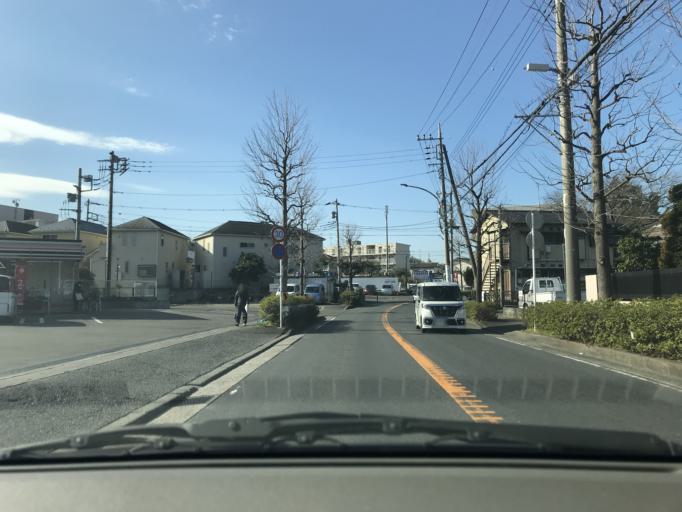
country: JP
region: Tokyo
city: Chofugaoka
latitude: 35.5969
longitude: 139.5622
